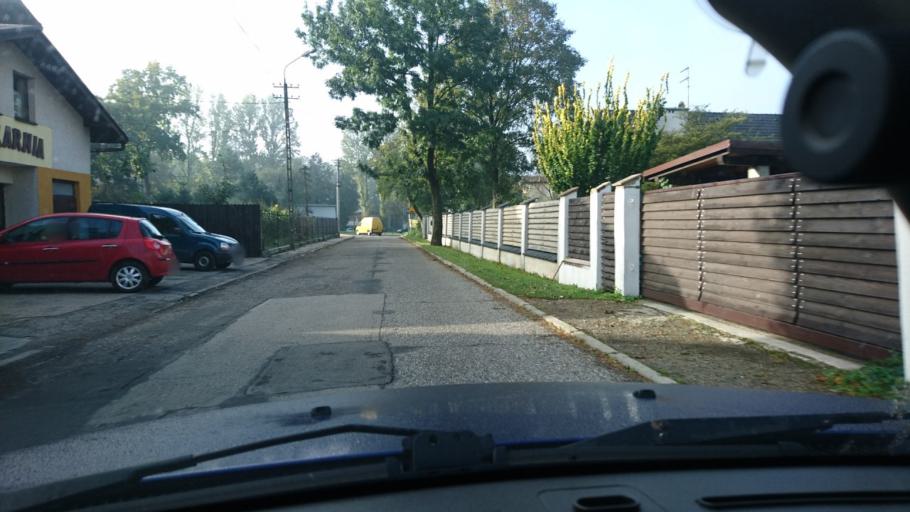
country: PL
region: Silesian Voivodeship
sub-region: Bielsko-Biala
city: Bielsko-Biala
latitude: 49.8015
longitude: 19.0623
